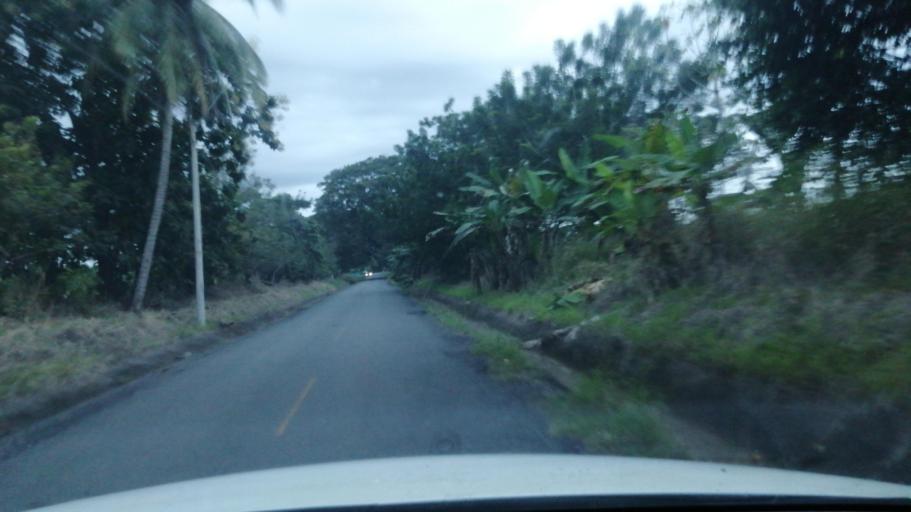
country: PA
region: Chiriqui
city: Alanje
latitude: 8.3976
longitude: -82.4969
